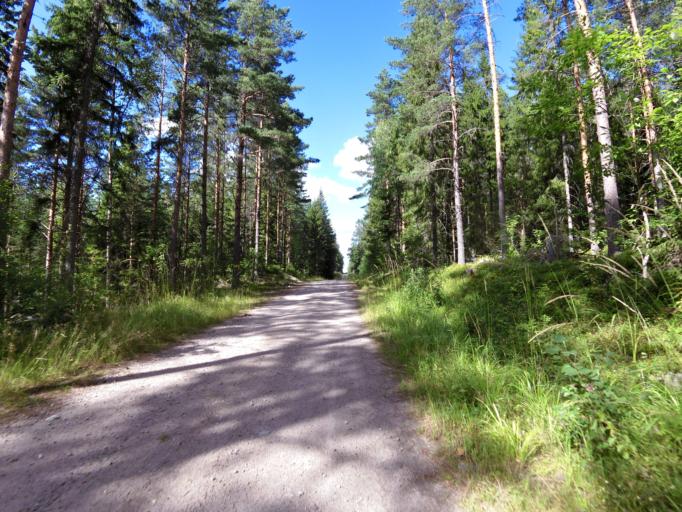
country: SE
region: Dalarna
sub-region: Faluns Kommun
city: Svardsjo
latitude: 60.6766
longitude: 15.9051
